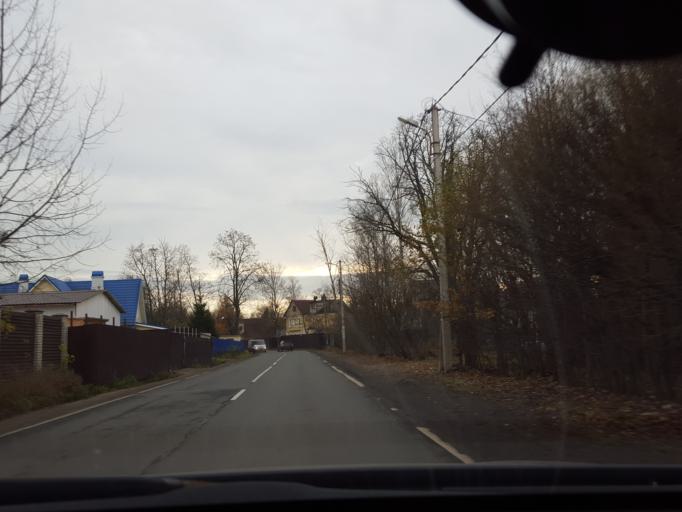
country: RU
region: St.-Petersburg
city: Shuvalovo
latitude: 60.0449
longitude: 30.2964
